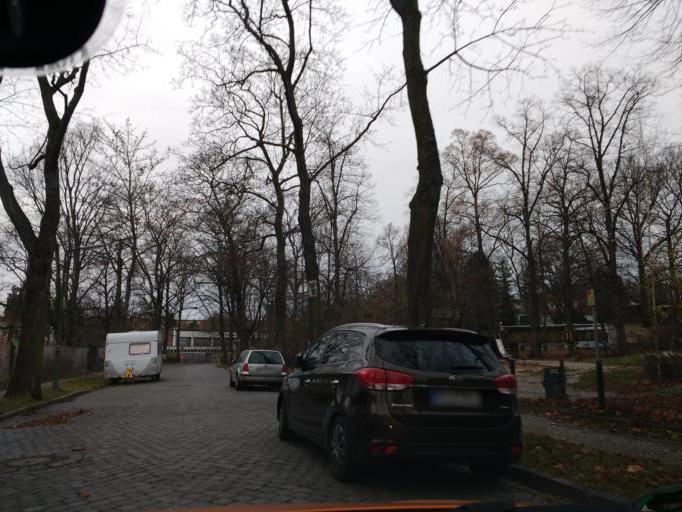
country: DE
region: Berlin
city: Schoneberg Bezirk
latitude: 52.4522
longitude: 13.3524
